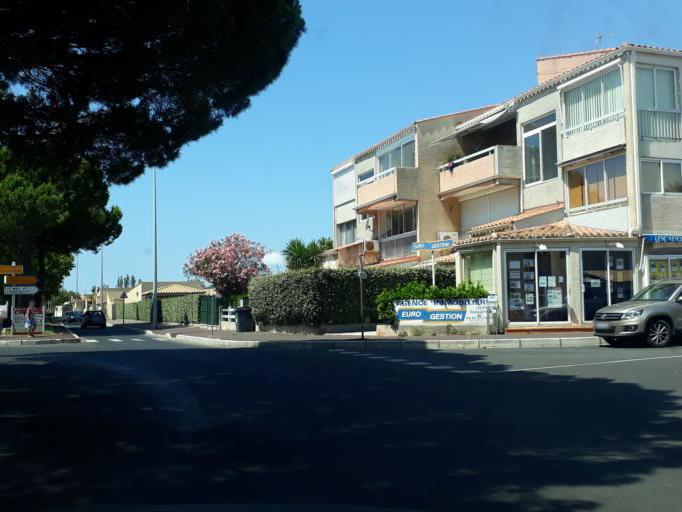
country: FR
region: Languedoc-Roussillon
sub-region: Departement de l'Herault
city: Le Cap d'Agde
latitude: 43.2805
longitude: 3.4925
